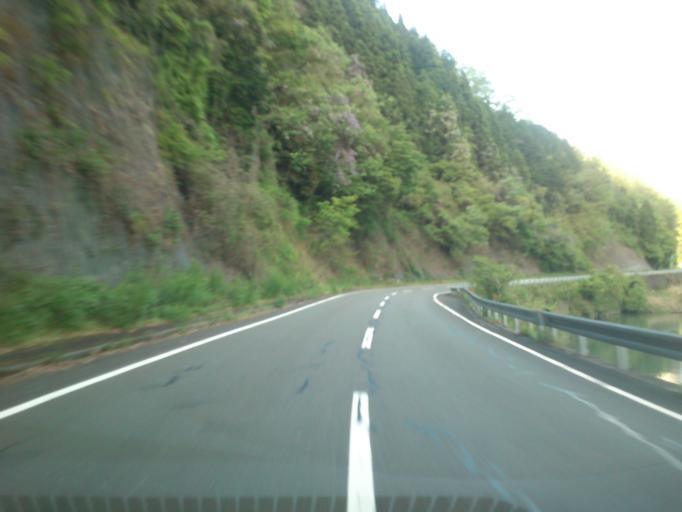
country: JP
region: Kyoto
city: Ayabe
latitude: 35.2772
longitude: 135.3574
